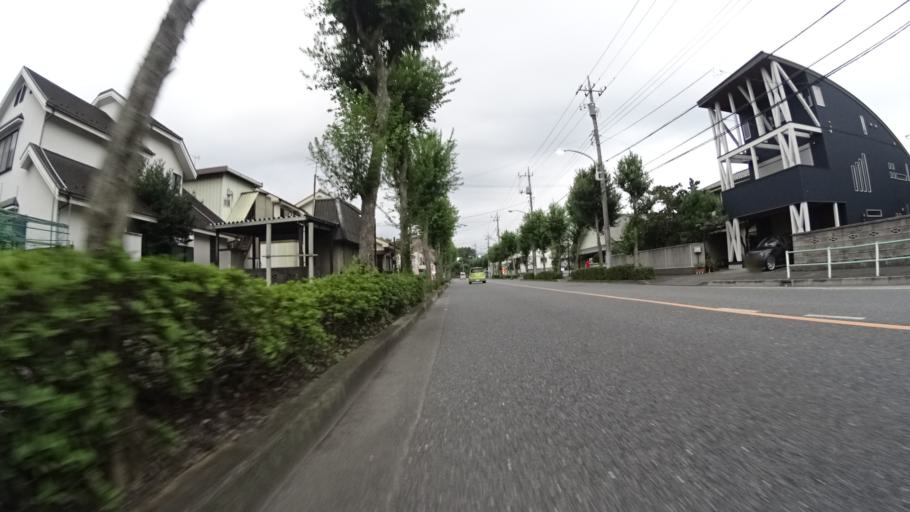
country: JP
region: Tokyo
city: Fussa
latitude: 35.7721
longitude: 139.2967
